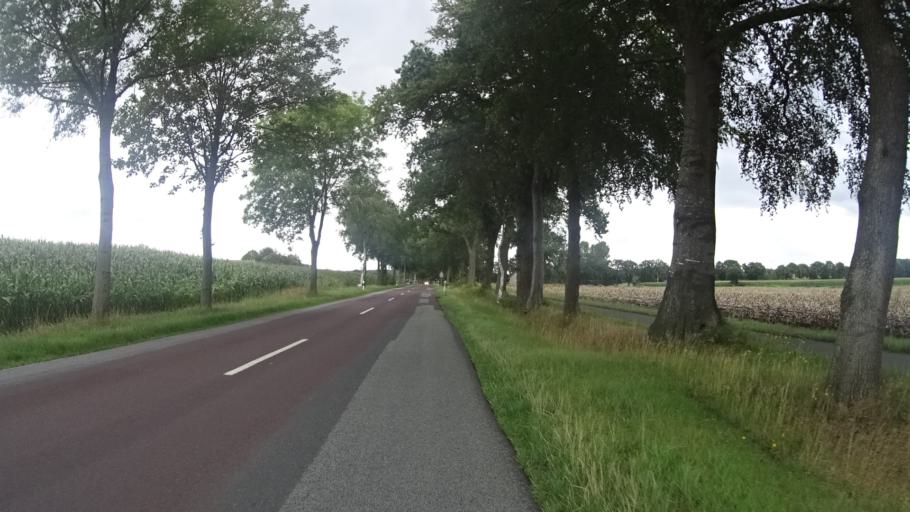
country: DE
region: Lower Saxony
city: Kuhrstedt
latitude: 53.6040
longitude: 8.8163
